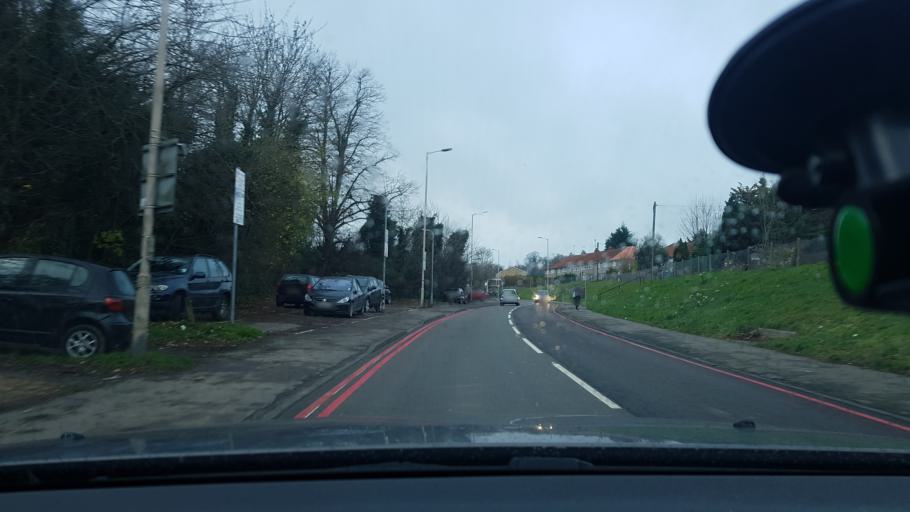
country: GB
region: England
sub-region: West Berkshire
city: Tilehurst
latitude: 51.4621
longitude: -1.0153
